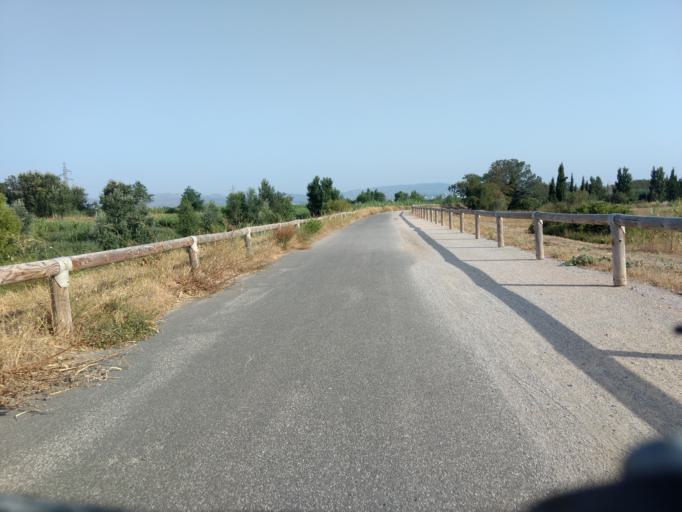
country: FR
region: Languedoc-Roussillon
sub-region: Departement des Pyrenees-Orientales
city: Pia
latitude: 42.7641
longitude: 2.9119
